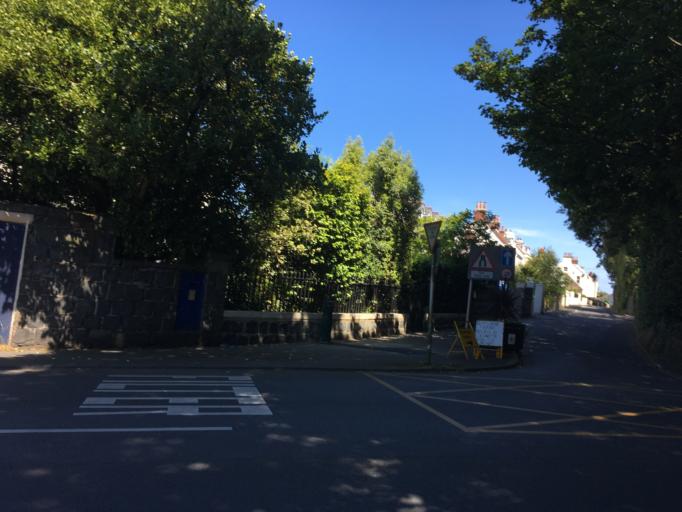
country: GG
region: St Peter Port
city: Saint Peter Port
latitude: 49.4586
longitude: -2.5531
